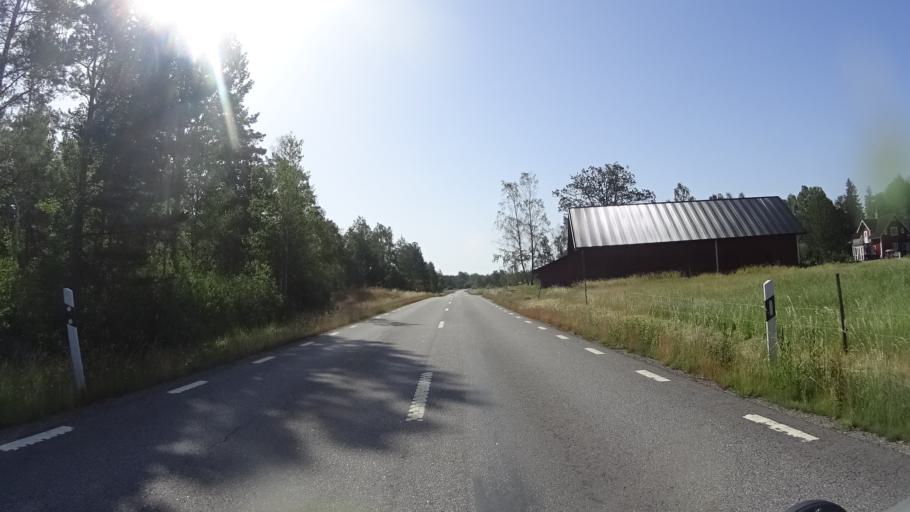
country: SE
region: OEstergoetland
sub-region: Atvidabergs Kommun
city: Atvidaberg
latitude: 58.0915
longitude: 16.1341
